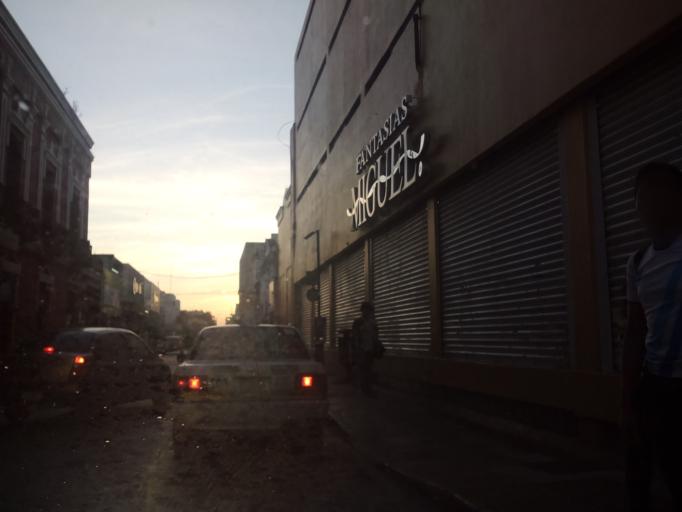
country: MX
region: Yucatan
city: Merida
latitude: 20.9685
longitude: -89.6216
